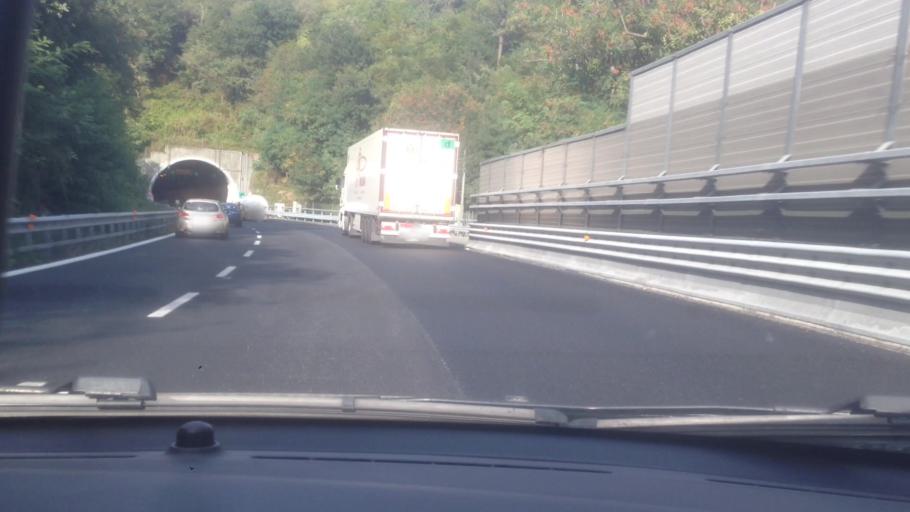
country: IT
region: Liguria
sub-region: Provincia di Genova
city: Cogoleto
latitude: 44.3927
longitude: 8.6551
